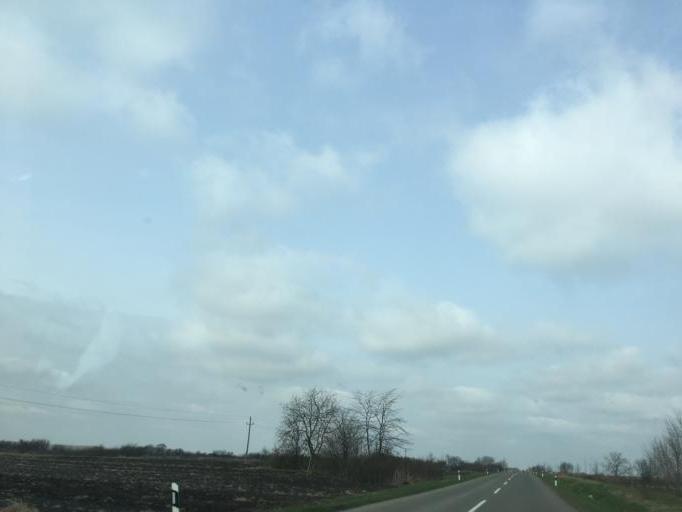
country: RS
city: Crepaja
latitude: 44.9566
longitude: 20.5852
